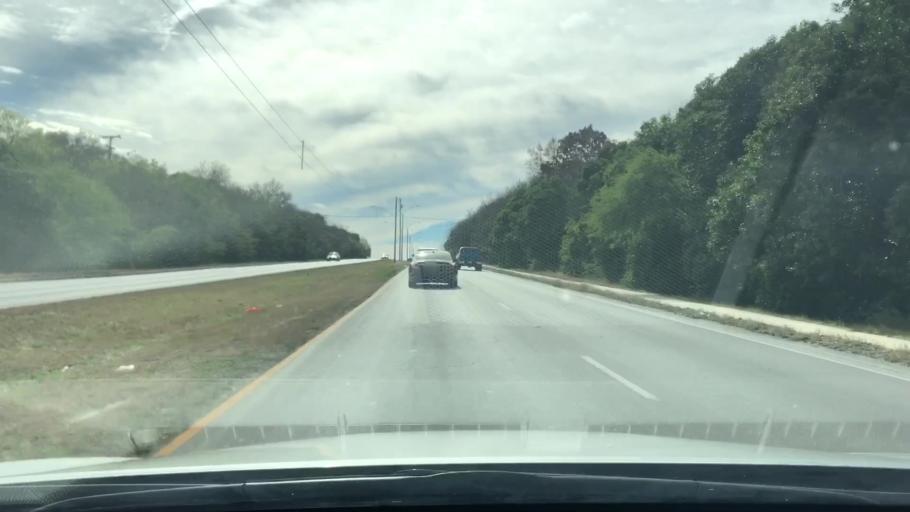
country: US
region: Texas
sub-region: Bexar County
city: Terrell Hills
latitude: 29.5016
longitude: -98.4346
